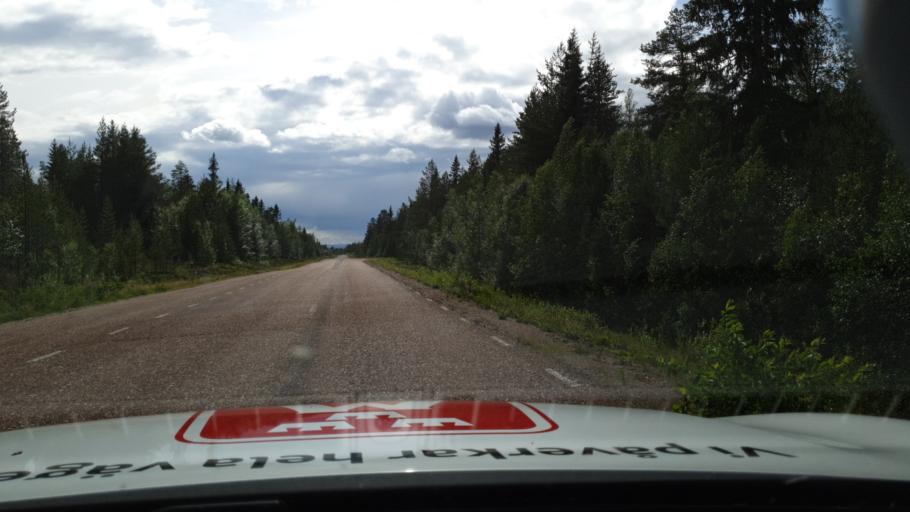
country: SE
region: Dalarna
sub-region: Alvdalens Kommun
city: AElvdalen
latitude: 61.7641
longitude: 13.4699
